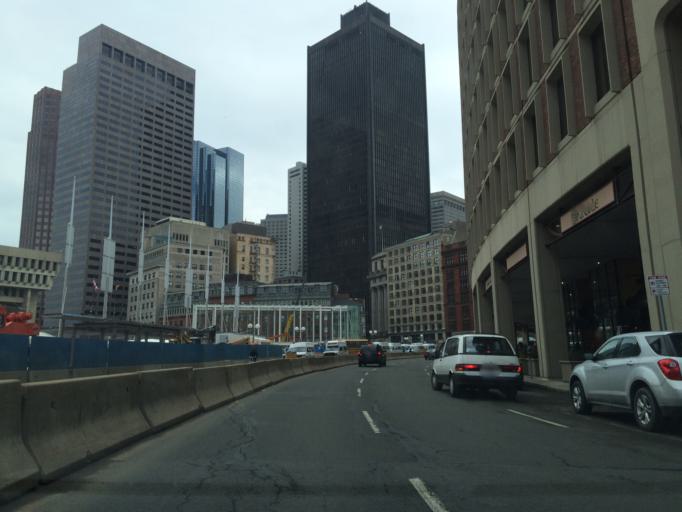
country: US
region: Massachusetts
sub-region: Suffolk County
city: Boston
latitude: 42.3606
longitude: -71.0607
